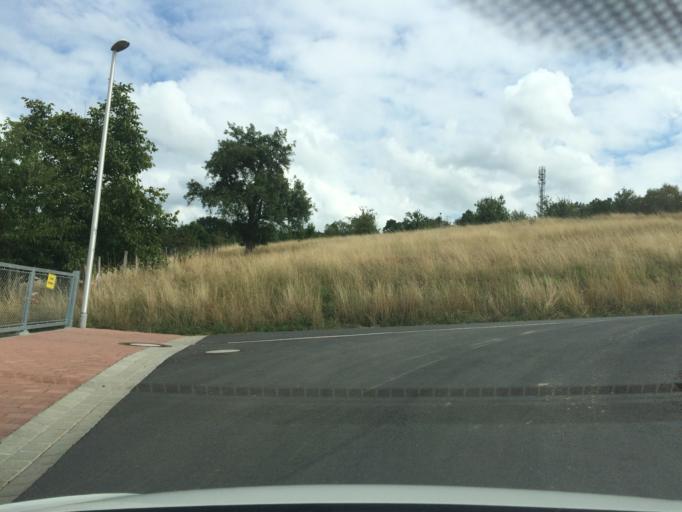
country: DE
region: Bavaria
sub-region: Regierungsbezirk Unterfranken
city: Sailauf
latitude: 50.0220
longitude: 9.2576
